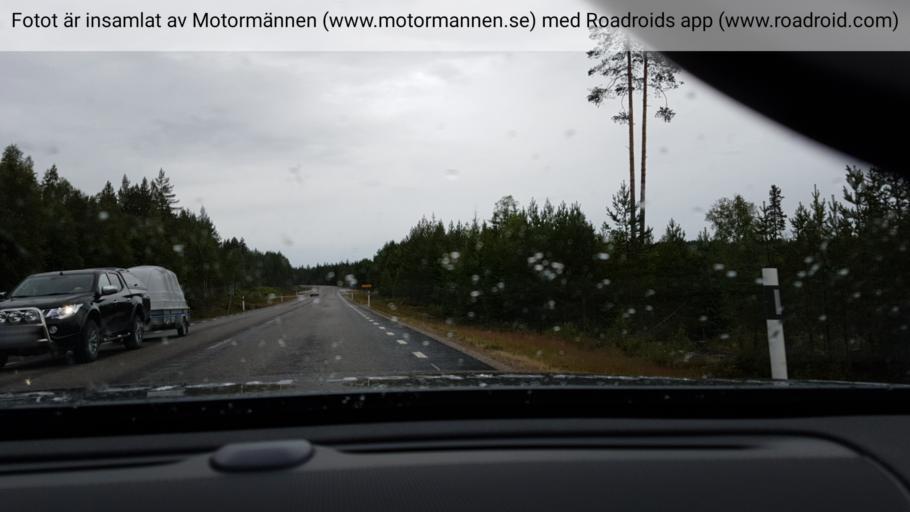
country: SE
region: Dalarna
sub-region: Rattviks Kommun
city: Raettvik
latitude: 60.8147
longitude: 15.2596
